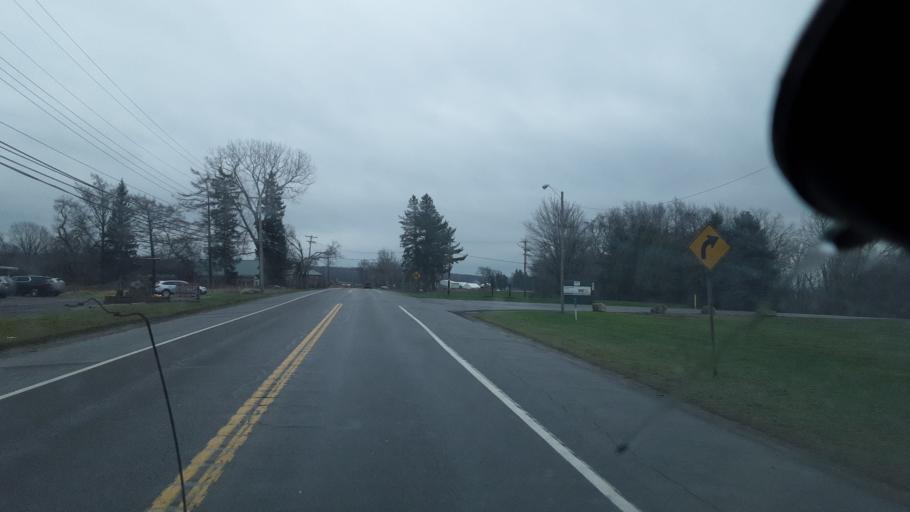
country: US
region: New York
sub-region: Cattaraugus County
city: Yorkshire
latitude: 42.5813
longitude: -78.4839
